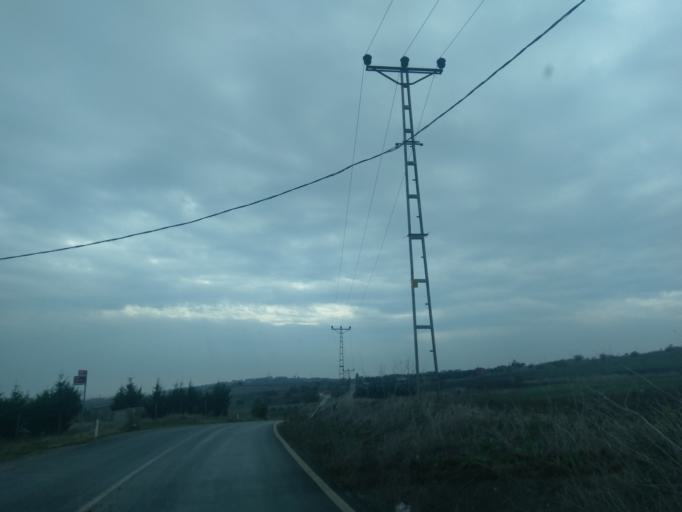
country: TR
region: Istanbul
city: Canta
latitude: 41.1077
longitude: 28.0795
